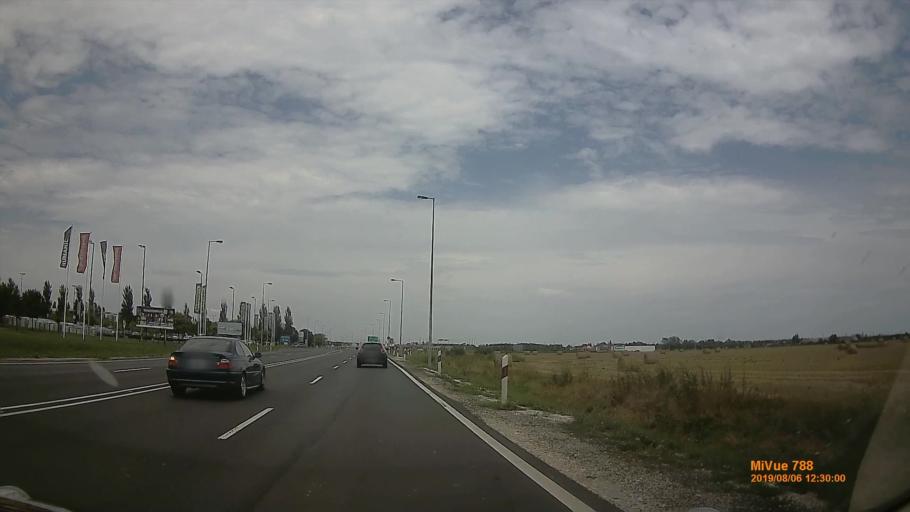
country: HU
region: Vas
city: Szombathely
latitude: 47.2367
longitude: 16.6561
